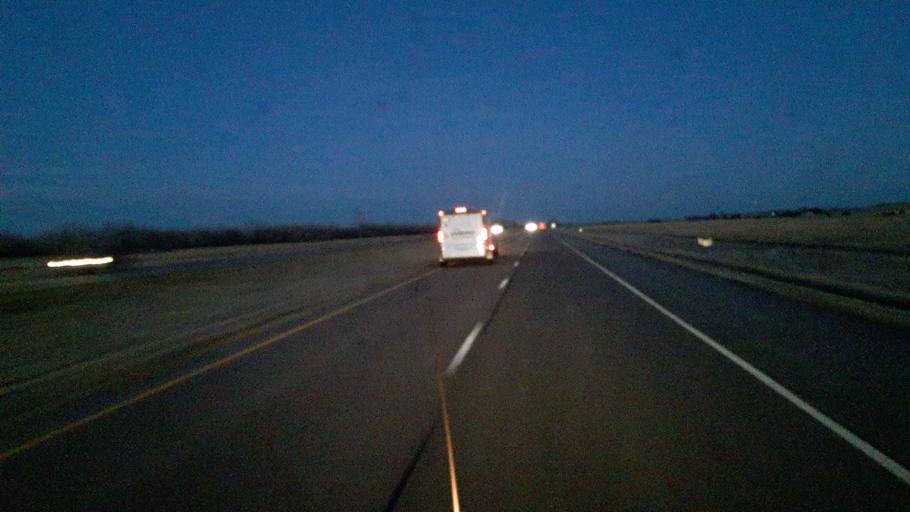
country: US
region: Nebraska
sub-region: Lincoln County
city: Sutherland
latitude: 41.1144
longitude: -101.3169
